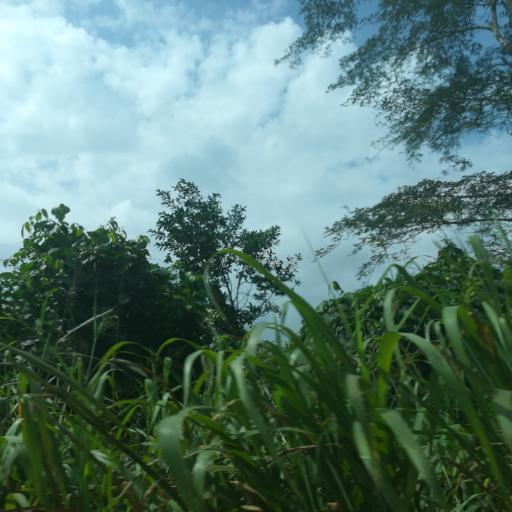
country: NG
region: Lagos
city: Ikorodu
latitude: 6.6631
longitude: 3.6301
